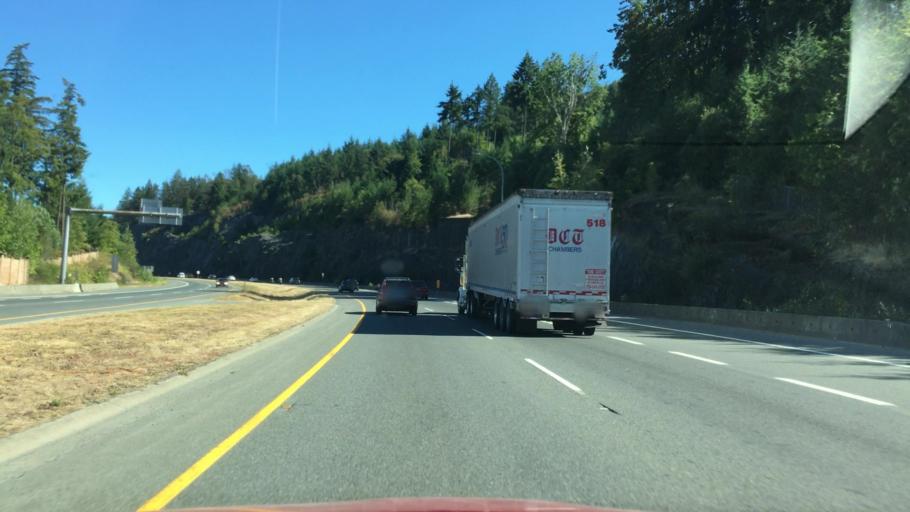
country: CA
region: British Columbia
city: Nanaimo
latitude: 49.1669
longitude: -123.9814
